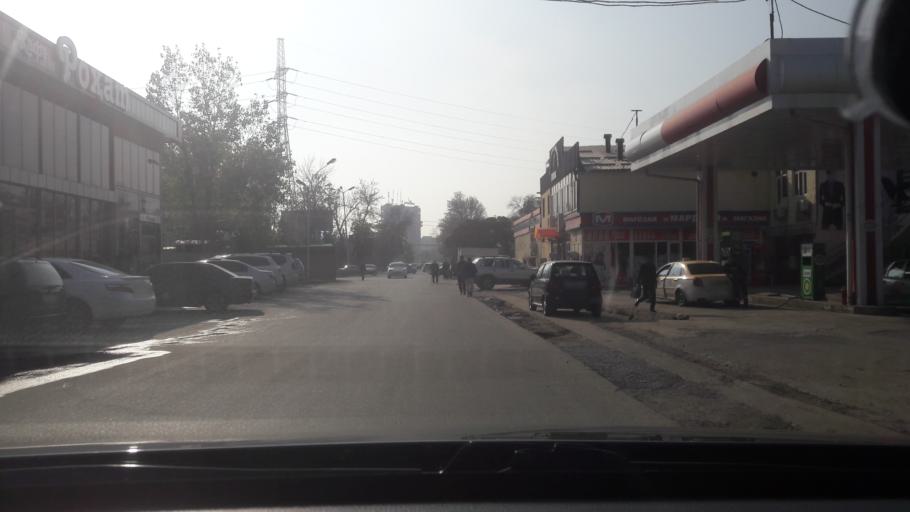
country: TJ
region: Dushanbe
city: Dushanbe
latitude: 38.5623
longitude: 68.7764
